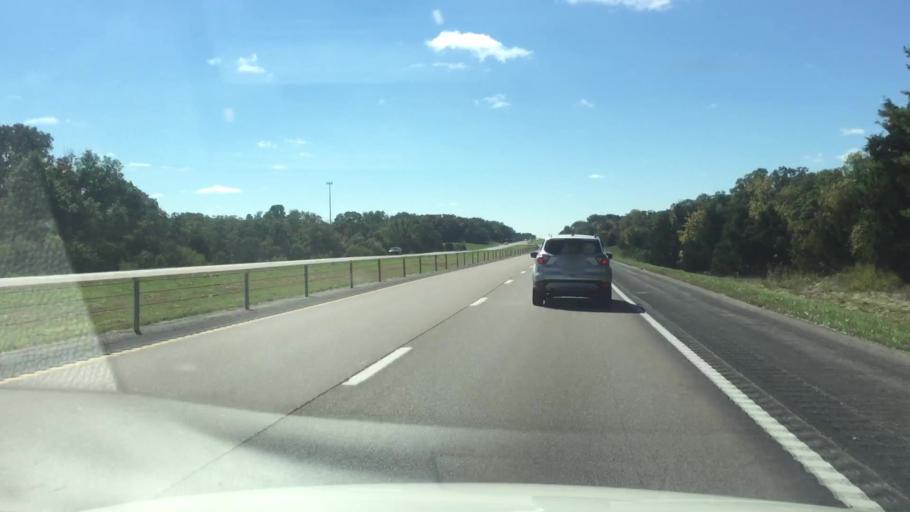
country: US
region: Missouri
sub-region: Boone County
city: Ashland
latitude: 38.7361
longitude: -92.2540
